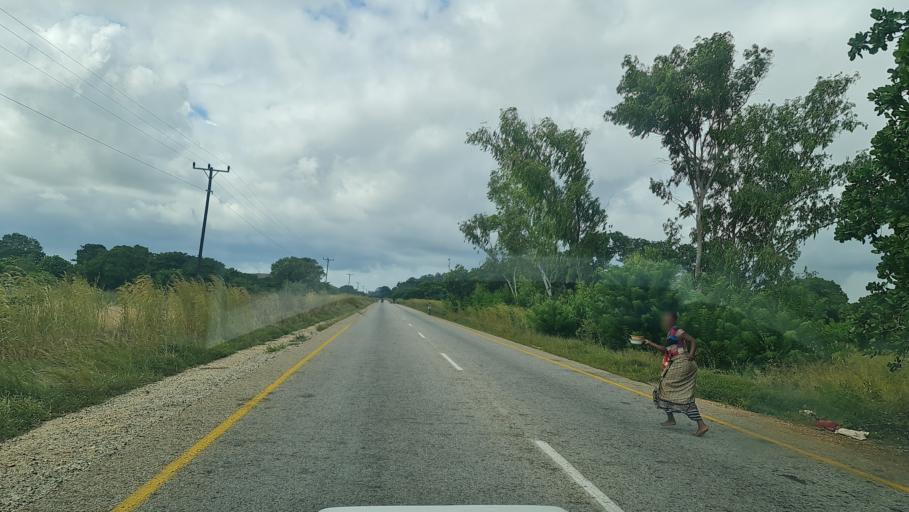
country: MZ
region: Nampula
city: Nampula
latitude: -14.9984
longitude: 39.6964
